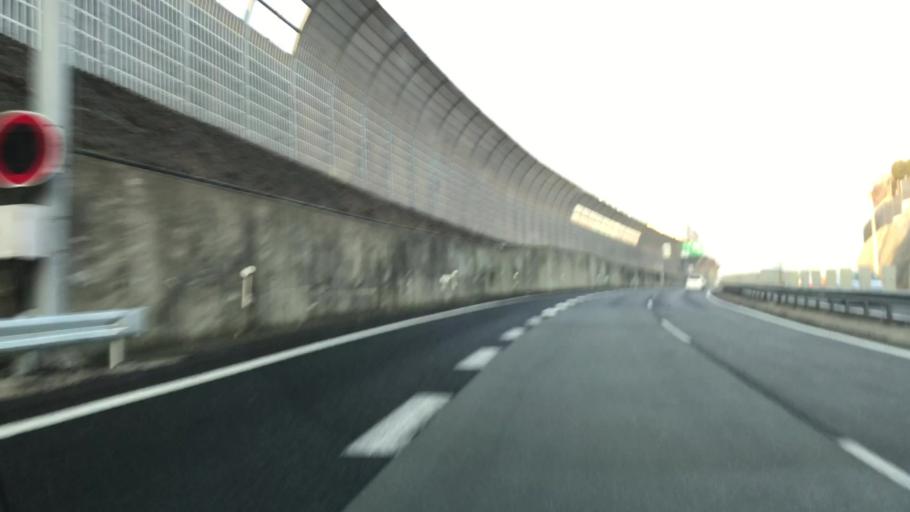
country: JP
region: Hyogo
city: Akashi
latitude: 34.6466
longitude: 135.0573
